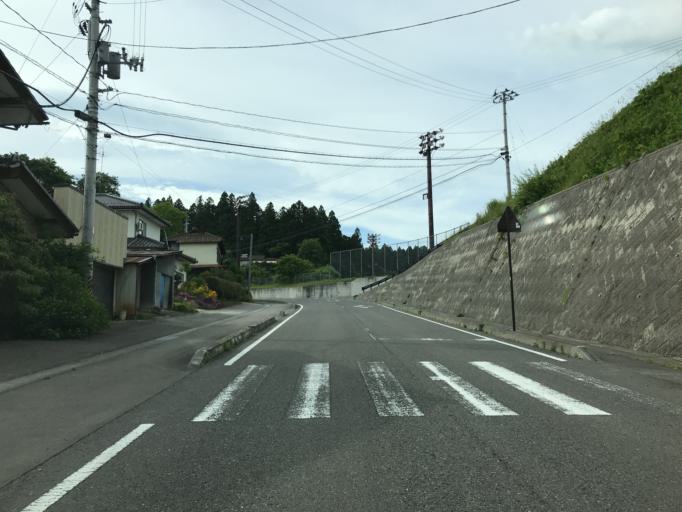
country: JP
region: Fukushima
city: Funehikimachi-funehiki
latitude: 37.5253
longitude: 140.5629
